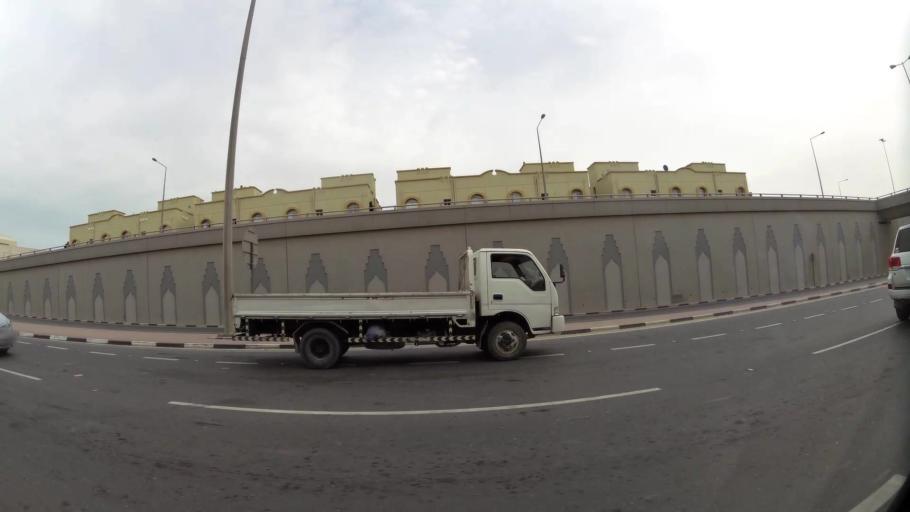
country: QA
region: Baladiyat ar Rayyan
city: Ar Rayyan
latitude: 25.3325
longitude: 51.4654
